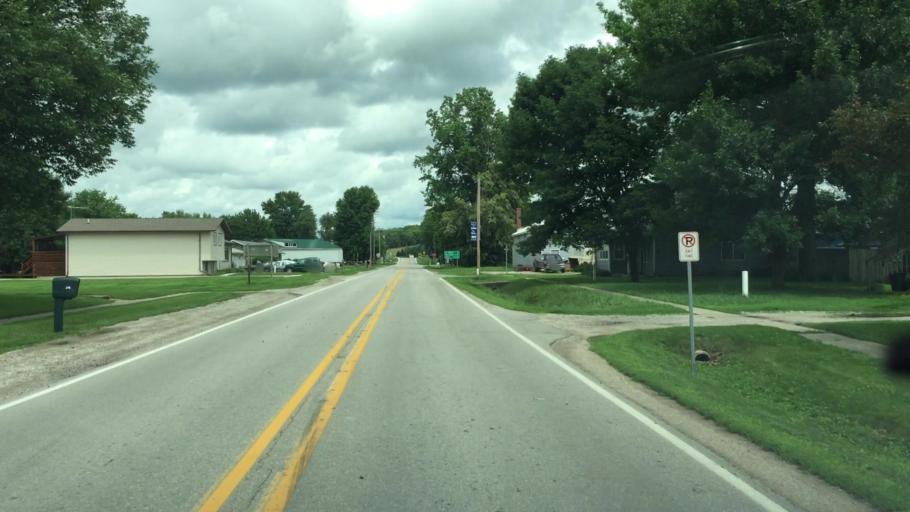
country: US
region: Iowa
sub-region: Jasper County
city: Monroe
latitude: 41.5773
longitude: -93.0234
